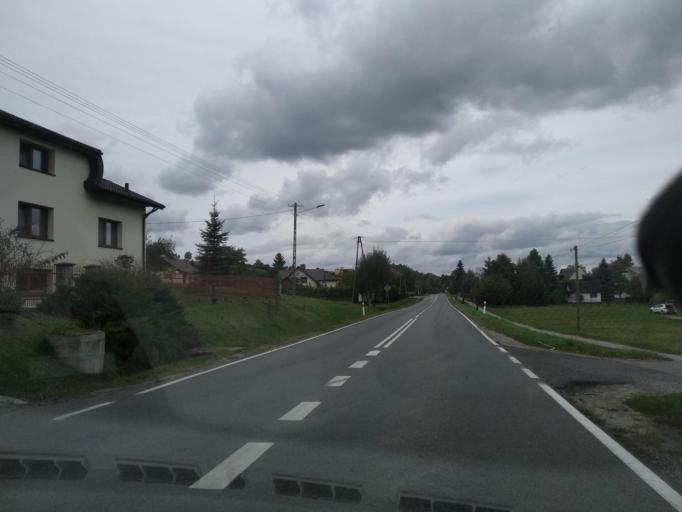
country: PL
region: Lesser Poland Voivodeship
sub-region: Powiat gorlicki
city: Sekowa
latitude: 49.6126
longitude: 21.2058
